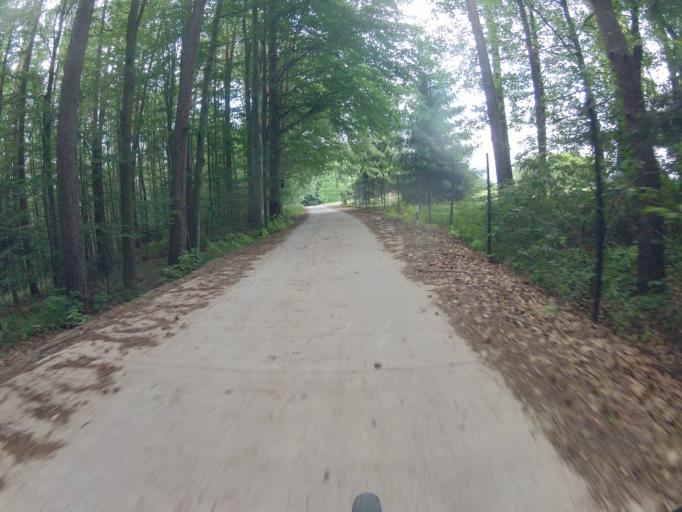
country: PL
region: Lesser Poland Voivodeship
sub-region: Powiat nowosadecki
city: Stary Sacz
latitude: 49.5618
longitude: 20.6256
